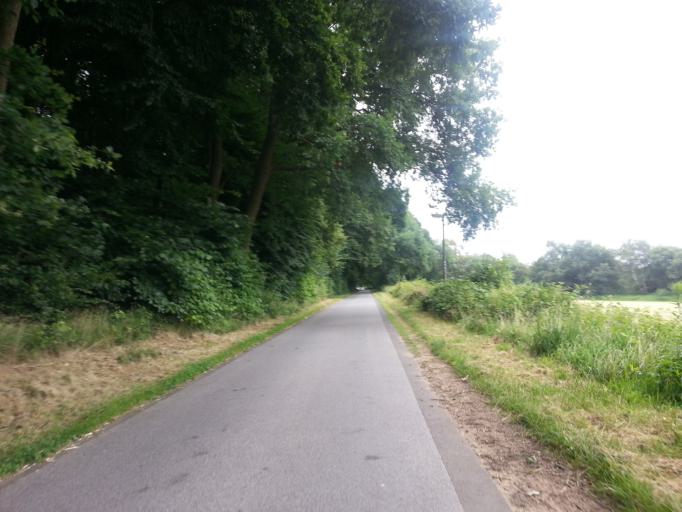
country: DE
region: North Rhine-Westphalia
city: Oer-Erkenschwick
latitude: 51.6573
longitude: 7.2377
